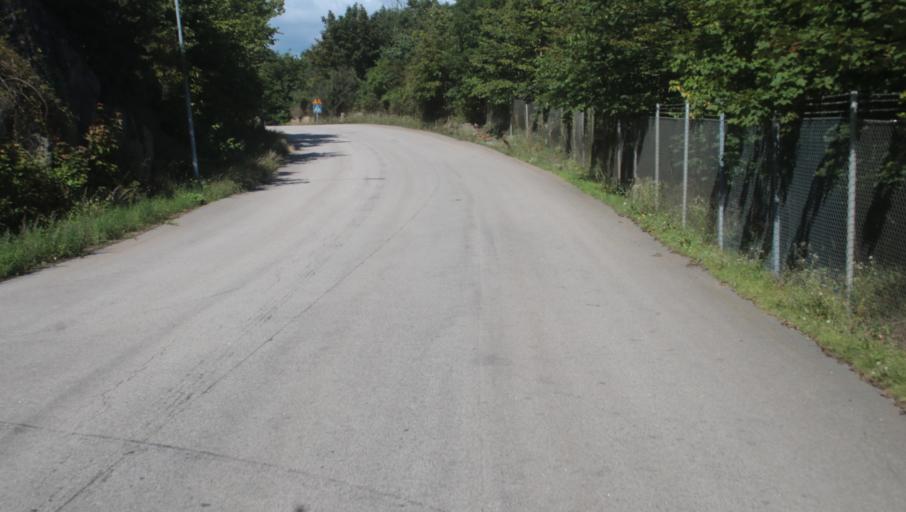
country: SE
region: Blekinge
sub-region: Karlshamns Kommun
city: Karlshamn
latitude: 56.1609
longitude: 14.8565
